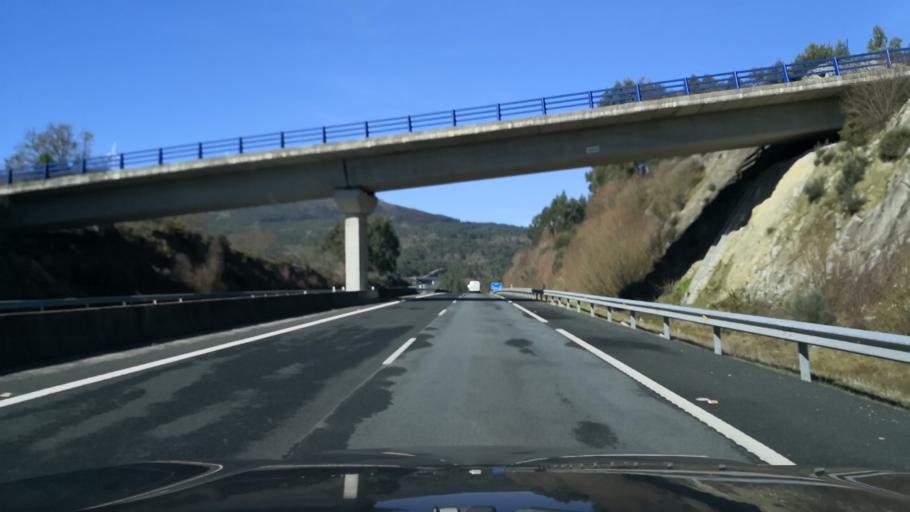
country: ES
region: Galicia
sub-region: Provincia de Ourense
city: Pinor
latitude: 42.4899
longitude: -8.0237
